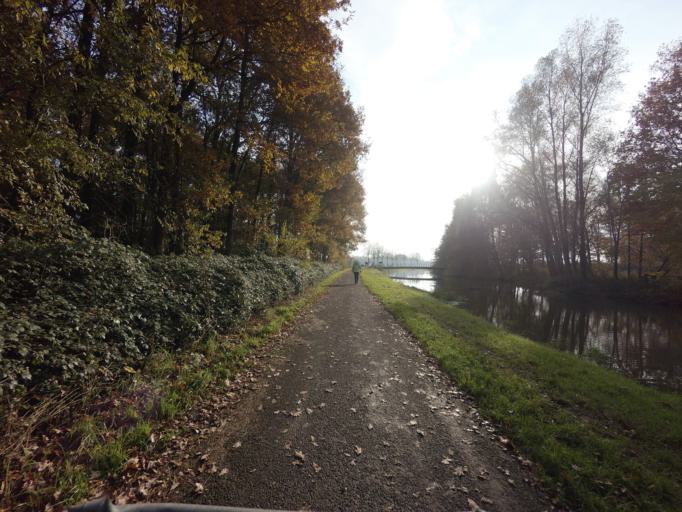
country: NL
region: North Brabant
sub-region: Gemeente Breda
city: Breda
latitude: 51.5411
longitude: 4.7813
